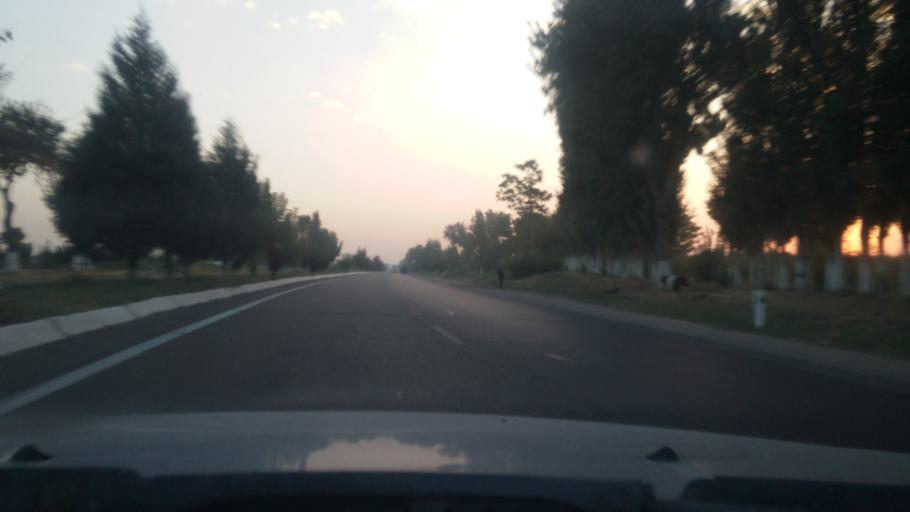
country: UZ
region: Toshkent
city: Zafar
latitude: 41.0021
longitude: 68.8240
